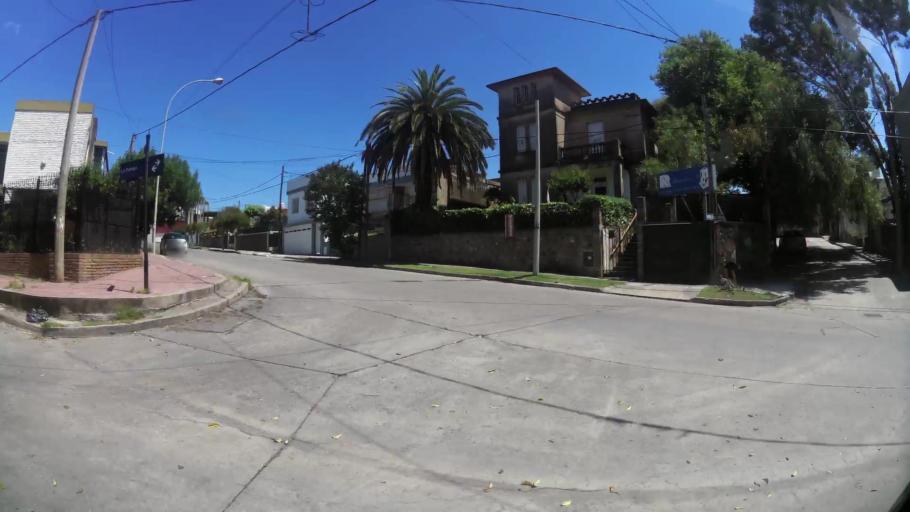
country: AR
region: Cordoba
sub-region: Departamento de Capital
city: Cordoba
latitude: -31.4142
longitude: -64.2036
